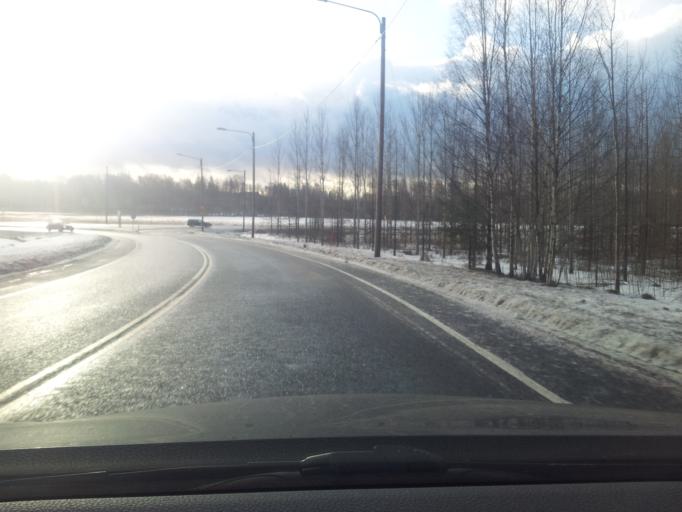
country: FI
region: Uusimaa
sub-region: Helsinki
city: Espoo
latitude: 60.1893
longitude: 24.5751
